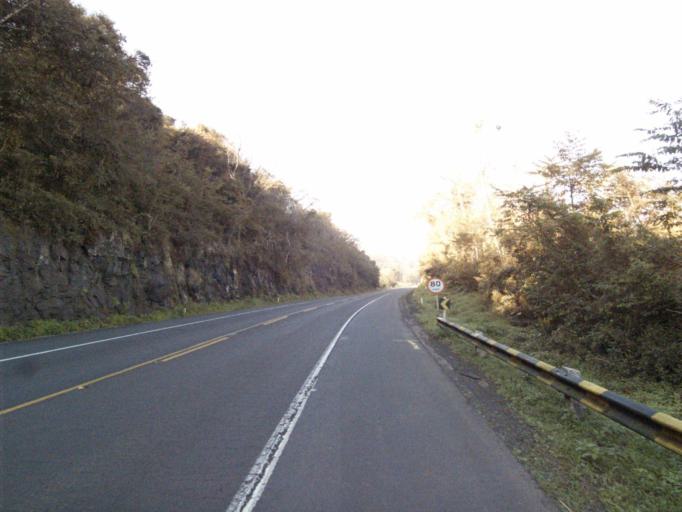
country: BR
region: Rio Grande do Sul
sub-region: Frederico Westphalen
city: Frederico Westphalen
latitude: -27.0051
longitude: -53.2251
